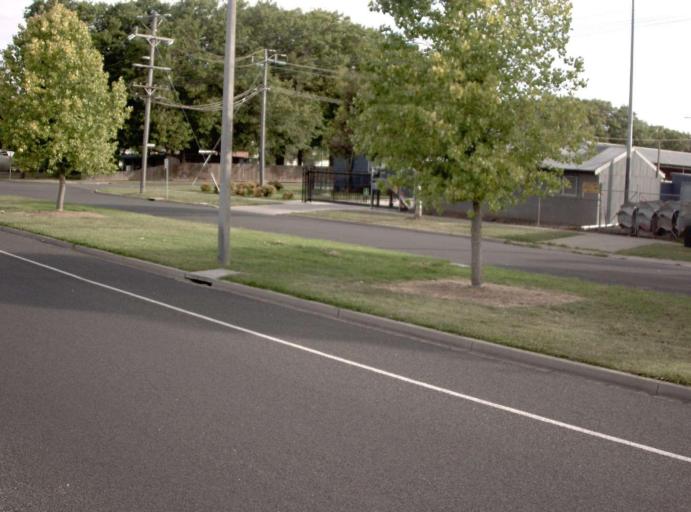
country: AU
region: Victoria
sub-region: Wellington
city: Sale
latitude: -37.9690
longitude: 146.9799
